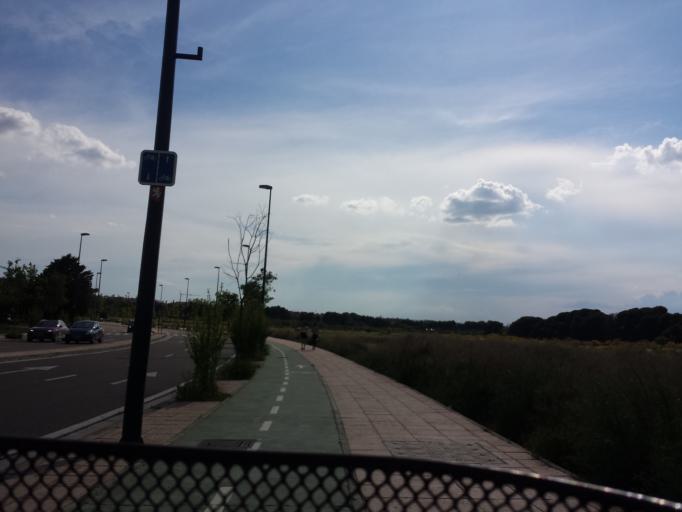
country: ES
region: Aragon
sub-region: Provincia de Zaragoza
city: Oliver-Valdefierro, Oliver, Valdefierro
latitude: 41.6343
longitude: -0.9261
